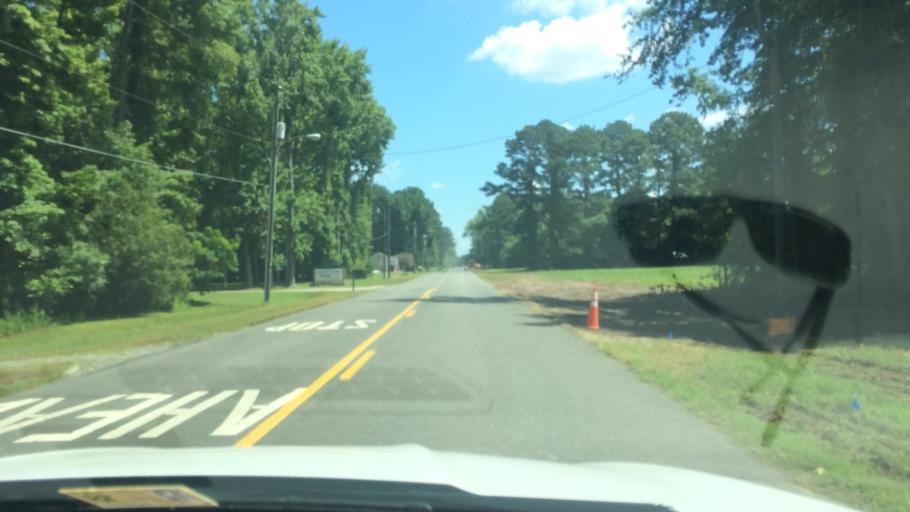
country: US
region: Virginia
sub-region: King William County
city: West Point
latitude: 37.5567
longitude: -76.8134
